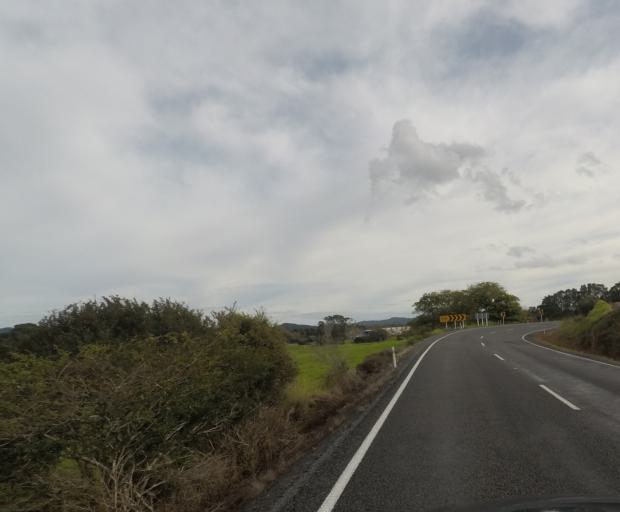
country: NZ
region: Northland
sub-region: Whangarei
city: Ruakaka
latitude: -35.9902
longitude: 174.4573
